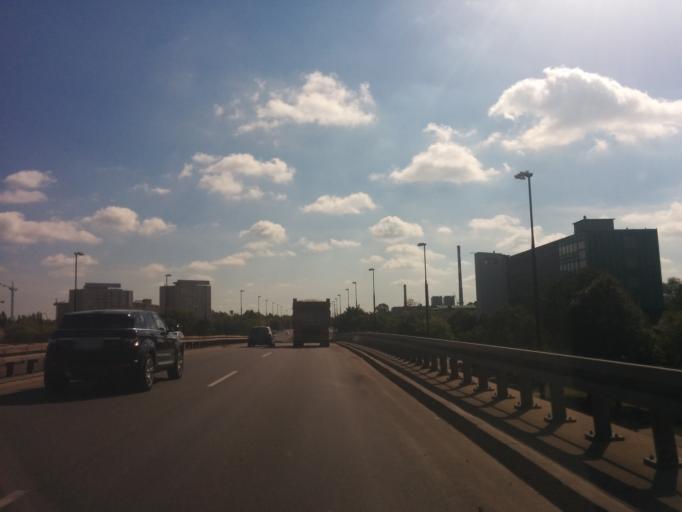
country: PL
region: Masovian Voivodeship
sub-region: Warszawa
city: Bialoleka
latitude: 52.3080
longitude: 20.9832
